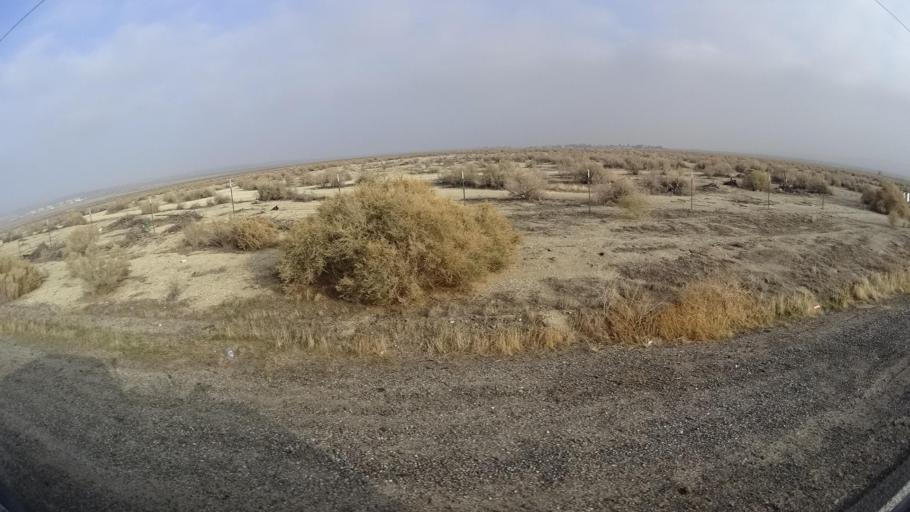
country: US
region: California
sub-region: Kern County
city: Ford City
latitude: 35.2172
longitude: -119.4456
